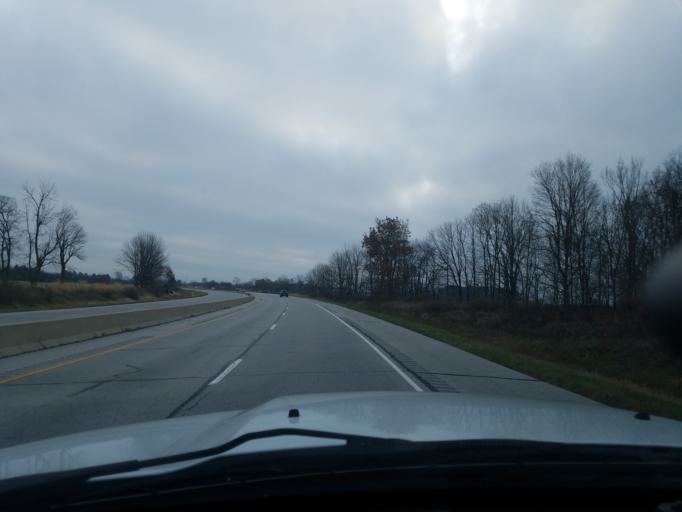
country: US
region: Indiana
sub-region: Delaware County
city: Yorktown
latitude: 40.2170
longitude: -85.5489
